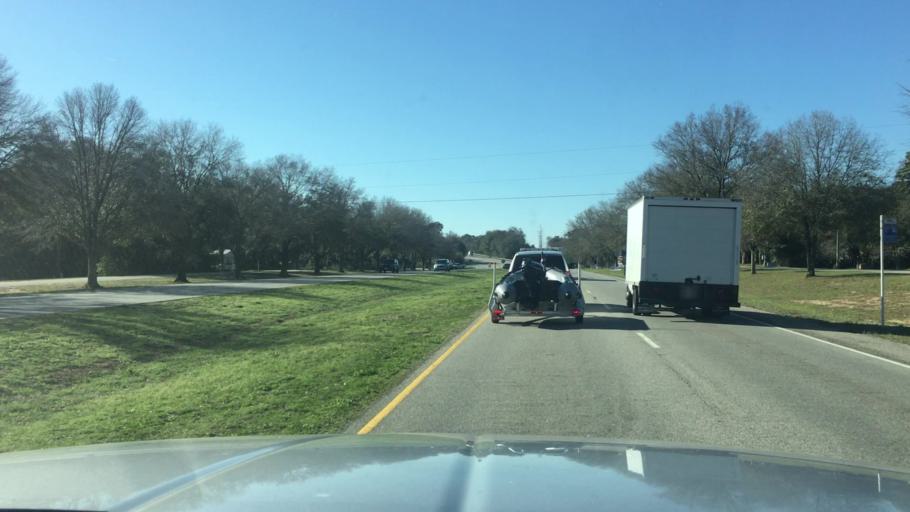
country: US
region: North Carolina
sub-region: New Hanover County
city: Sea Breeze
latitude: 34.0634
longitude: -77.8988
